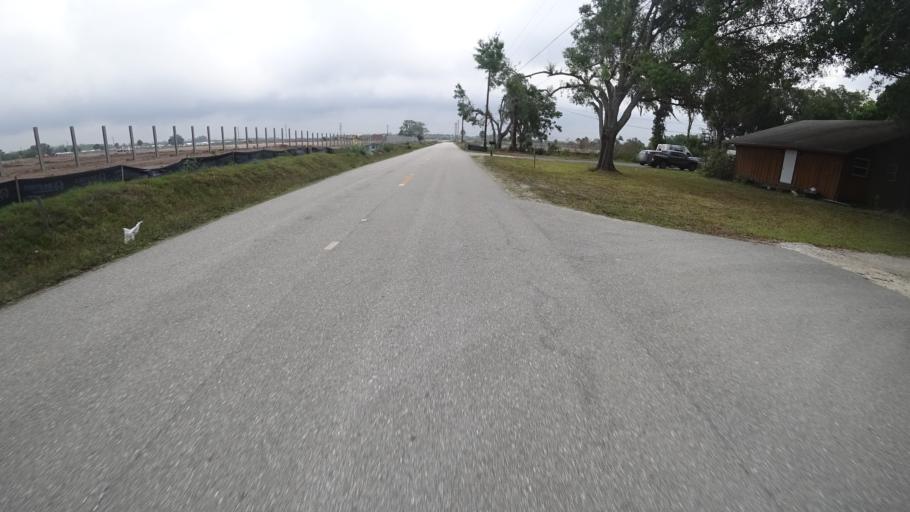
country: US
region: Florida
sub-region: Manatee County
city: Samoset
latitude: 27.4744
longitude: -82.5137
